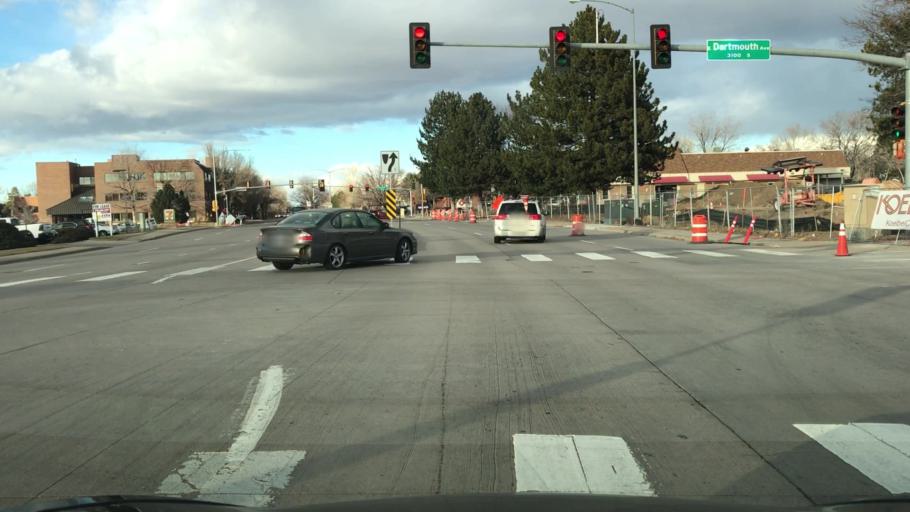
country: US
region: Colorado
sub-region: Adams County
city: Aurora
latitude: 39.6603
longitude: -104.8473
